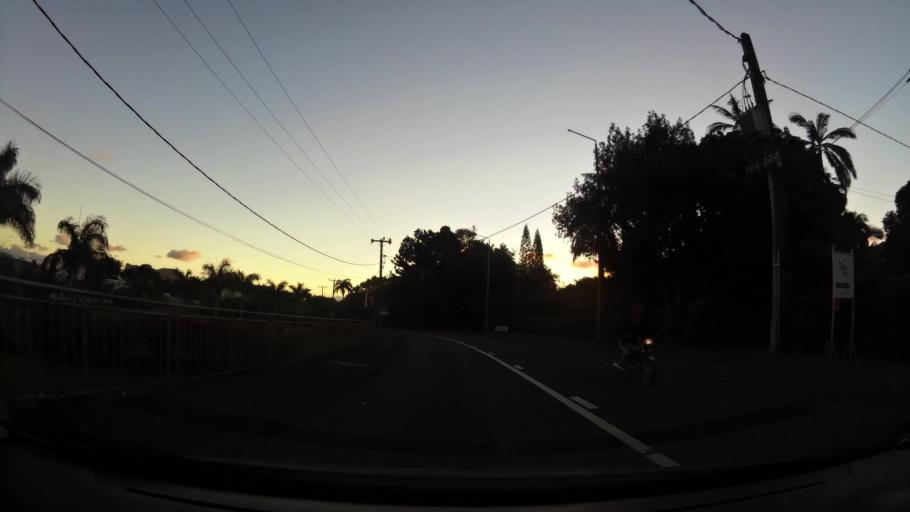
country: MU
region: Moka
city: Saint Pierre
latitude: -20.2239
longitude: 57.5133
